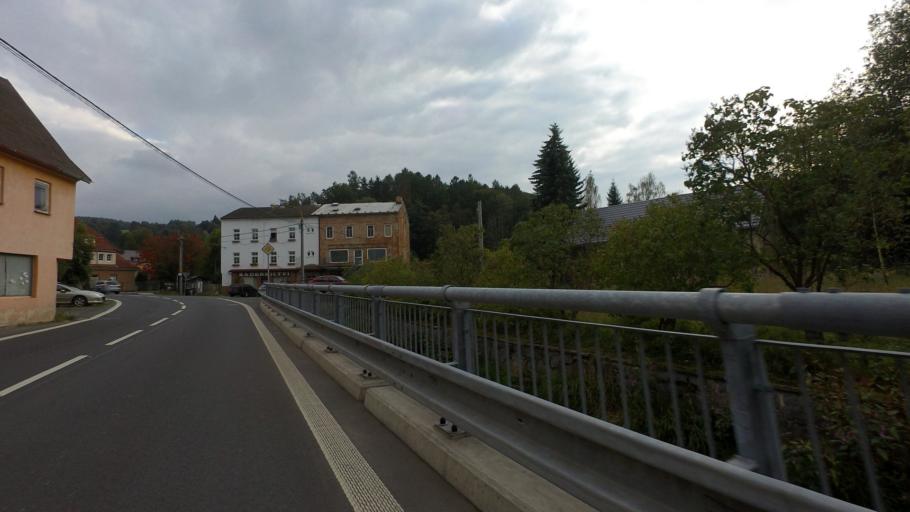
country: CZ
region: Ustecky
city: Dolni Poustevna
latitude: 50.9803
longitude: 14.2882
